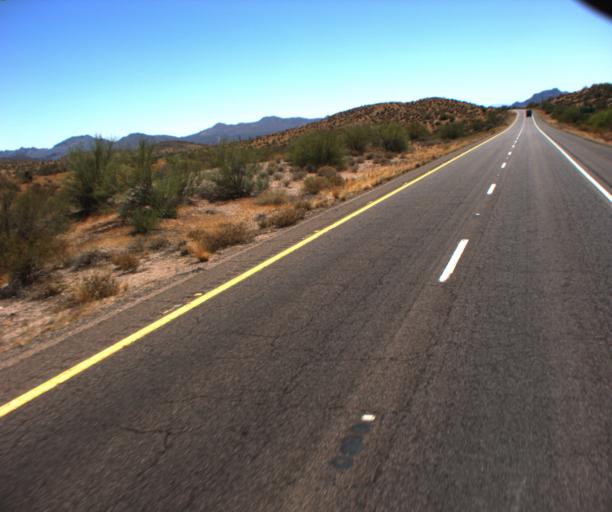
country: US
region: Arizona
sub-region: Maricopa County
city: Rio Verde
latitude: 33.6212
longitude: -111.5689
